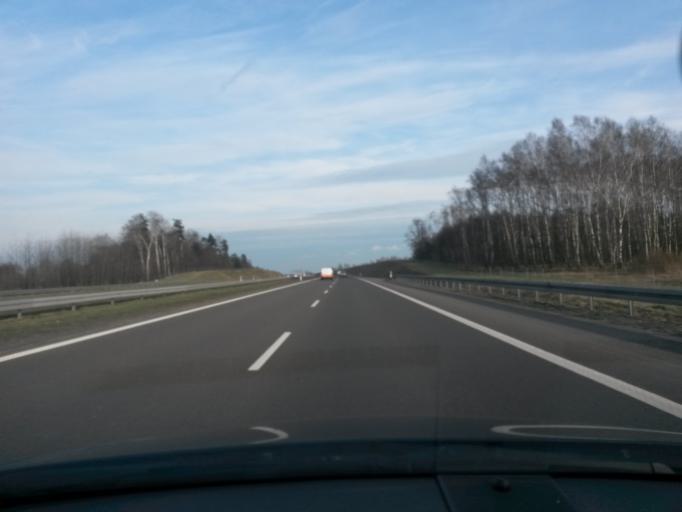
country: PL
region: Lodz Voivodeship
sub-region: Powiat zgierski
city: Zgierz
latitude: 51.9050
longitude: 19.4510
